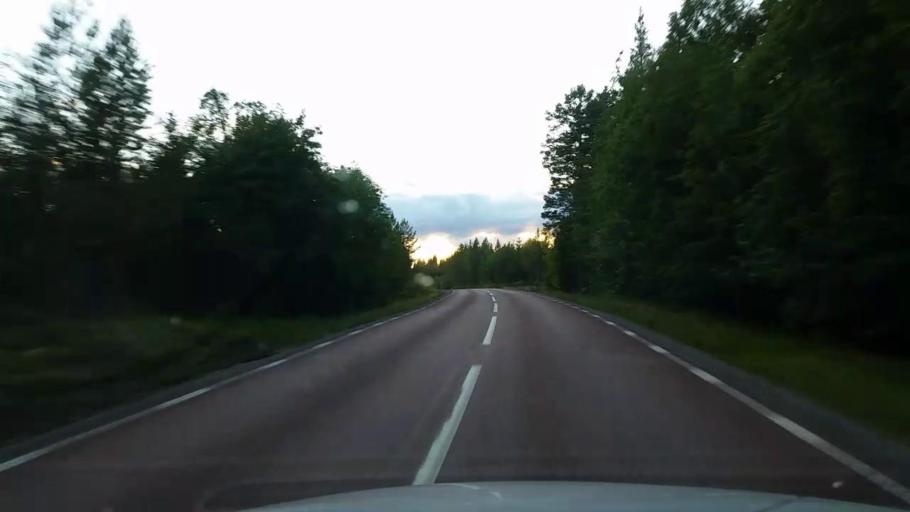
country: SE
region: Gaevleborg
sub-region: Ljusdals Kommun
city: Farila
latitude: 62.0986
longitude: 15.7901
